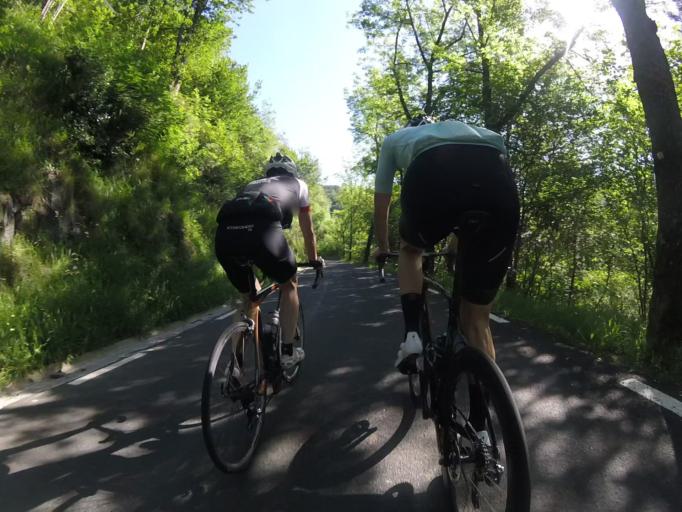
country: ES
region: Basque Country
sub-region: Provincia de Guipuzcoa
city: Beizama
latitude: 43.1342
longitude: -2.2058
